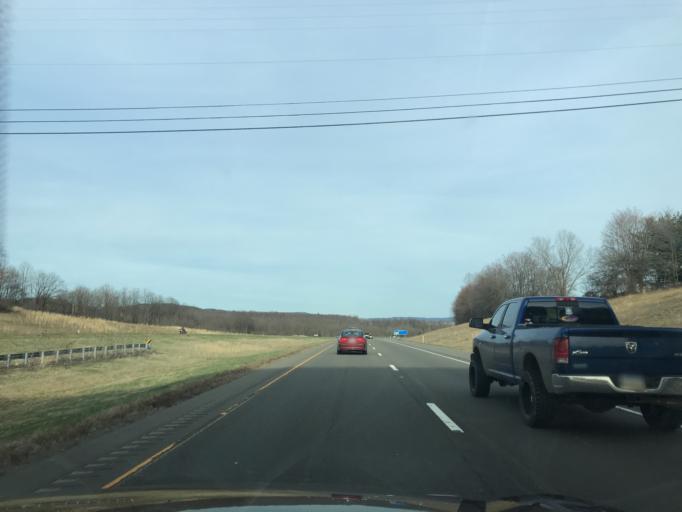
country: US
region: Pennsylvania
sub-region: Lycoming County
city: Montoursville
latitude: 41.2526
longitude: -76.8614
